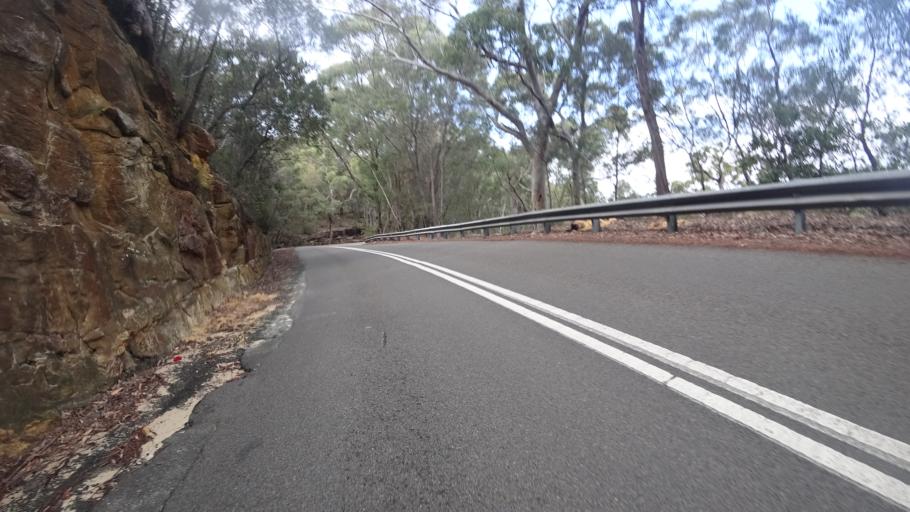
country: AU
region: New South Wales
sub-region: Hornsby Shire
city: Mount Colah
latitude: -33.6618
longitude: 151.1484
